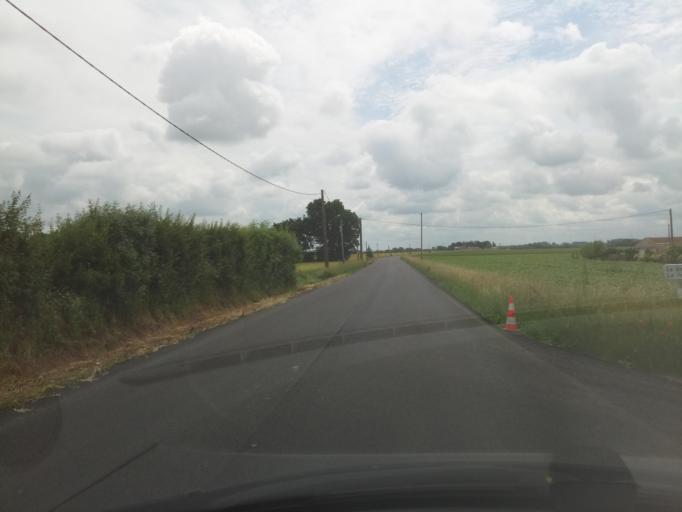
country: FR
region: Poitou-Charentes
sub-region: Departement de la Charente-Maritime
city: Saint-Jean-de-Liversay
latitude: 46.2810
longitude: -0.9190
